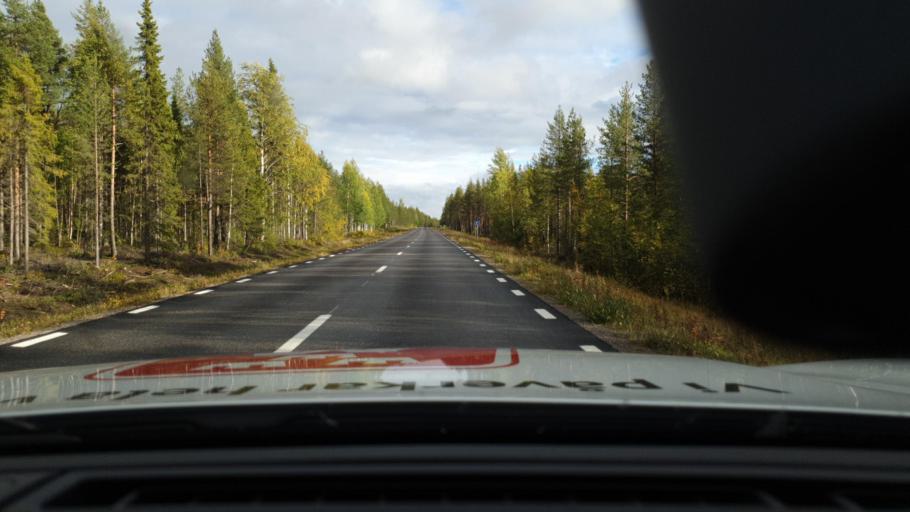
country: SE
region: Norrbotten
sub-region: Overkalix Kommun
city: OEverkalix
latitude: 66.9872
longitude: 22.5992
